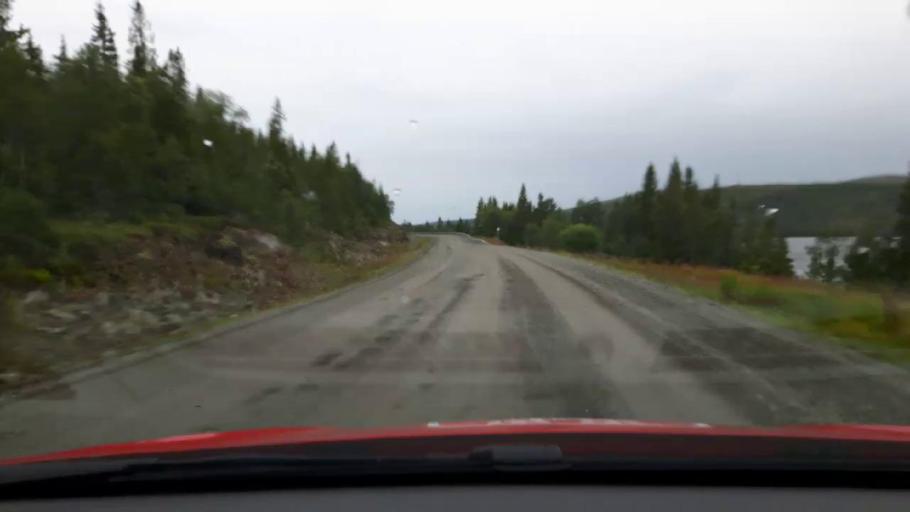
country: NO
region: Nord-Trondelag
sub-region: Meraker
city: Meraker
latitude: 63.5367
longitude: 12.3837
